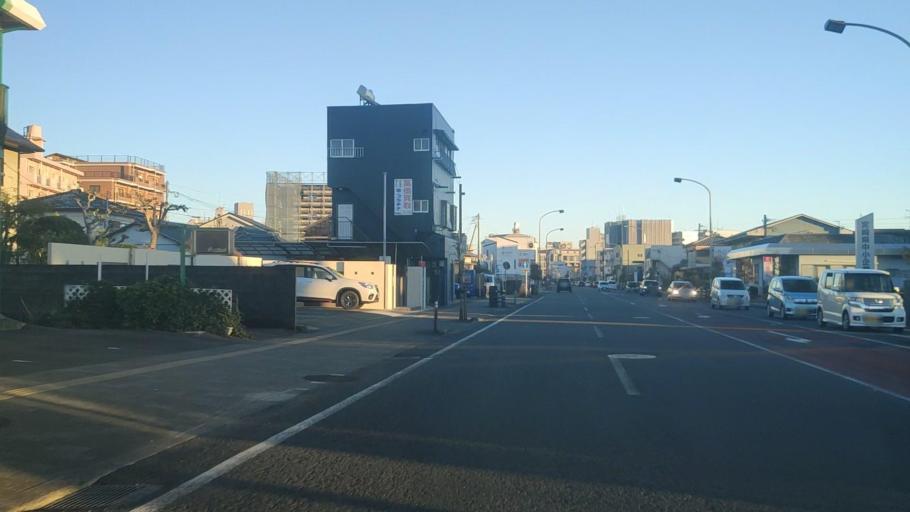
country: JP
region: Miyazaki
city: Miyazaki-shi
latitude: 31.9122
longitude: 131.4143
